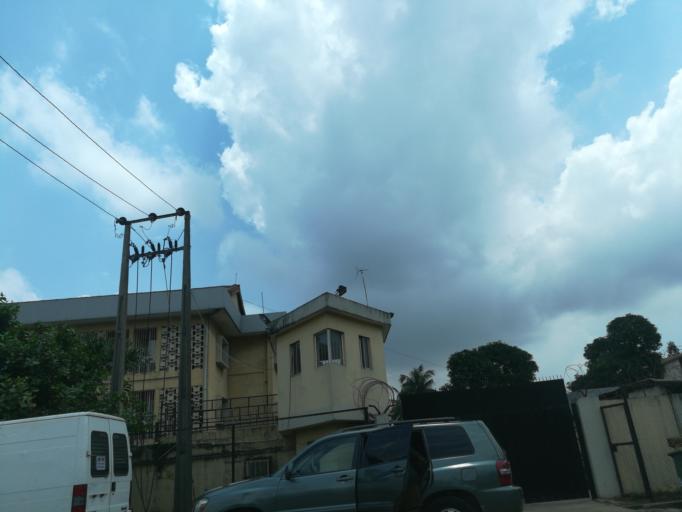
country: NG
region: Lagos
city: Oshodi
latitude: 6.5475
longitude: 3.3287
